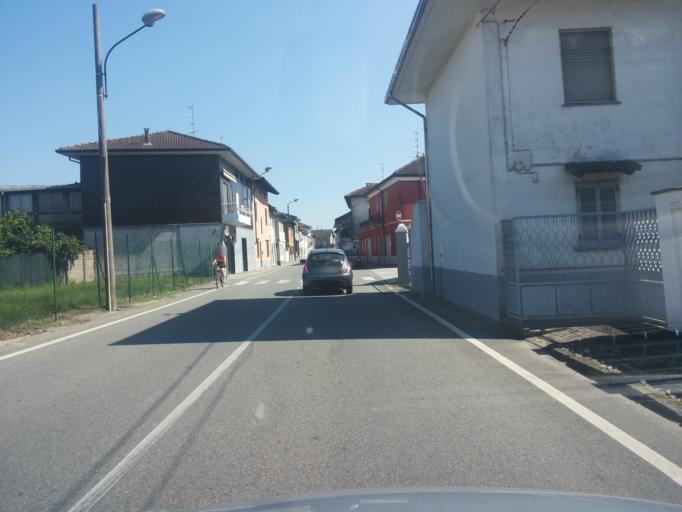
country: IT
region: Piedmont
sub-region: Provincia di Novara
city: Casalvolone
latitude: 45.4014
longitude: 8.4640
